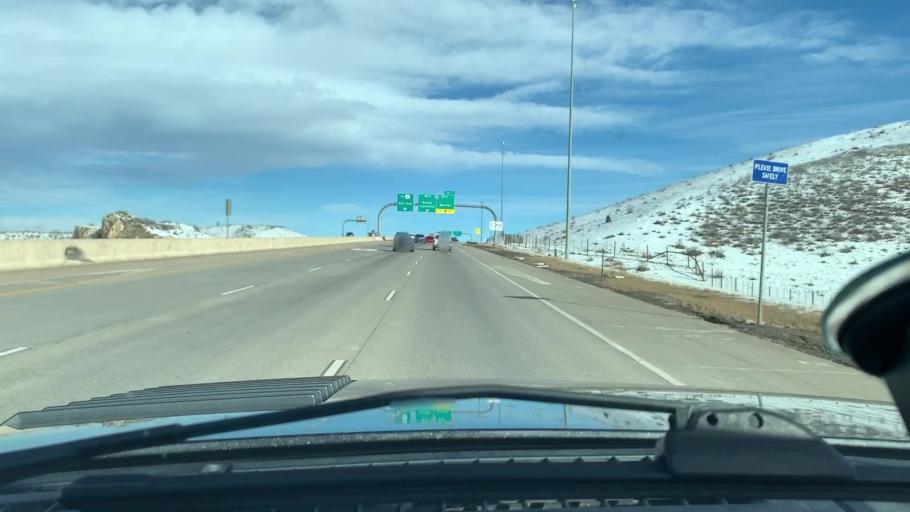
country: US
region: Colorado
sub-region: Jefferson County
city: West Pleasant View
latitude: 39.7036
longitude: -105.1932
